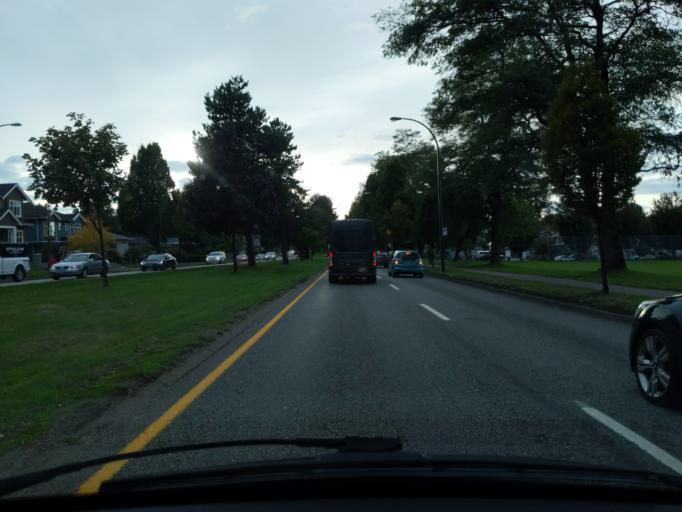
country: CA
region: British Columbia
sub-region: Fraser Valley Regional District
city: North Vancouver
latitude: 49.2696
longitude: -123.0502
